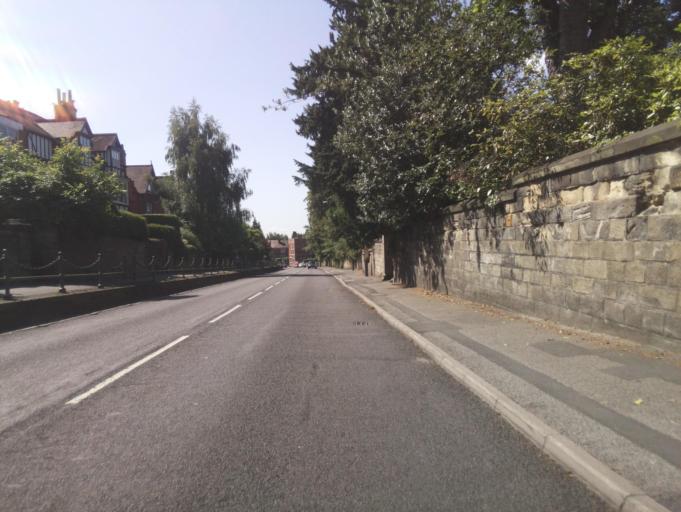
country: GB
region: England
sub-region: Derby
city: Derby
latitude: 52.9319
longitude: -1.4840
